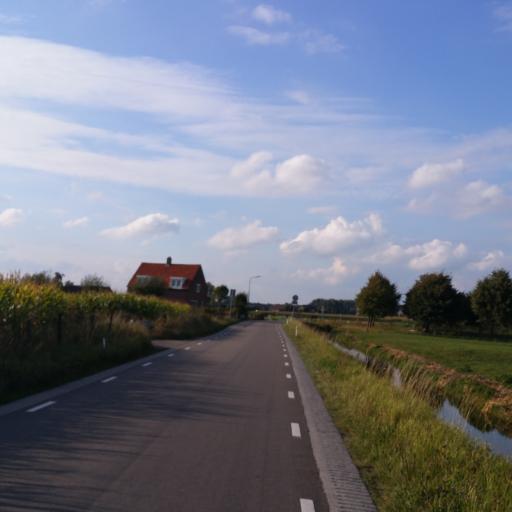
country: NL
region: Utrecht
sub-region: Gemeente IJsselstein
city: IJsselstein
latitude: 52.0429
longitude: 5.0113
